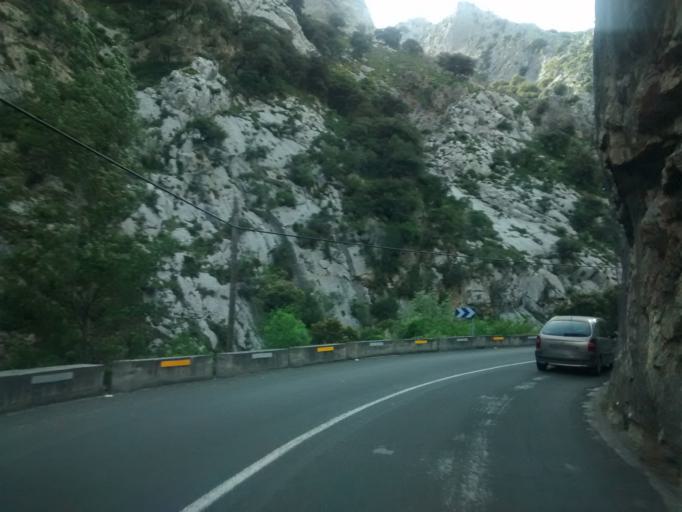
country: ES
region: Cantabria
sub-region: Provincia de Cantabria
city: Potes
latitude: 43.2036
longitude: -4.5932
